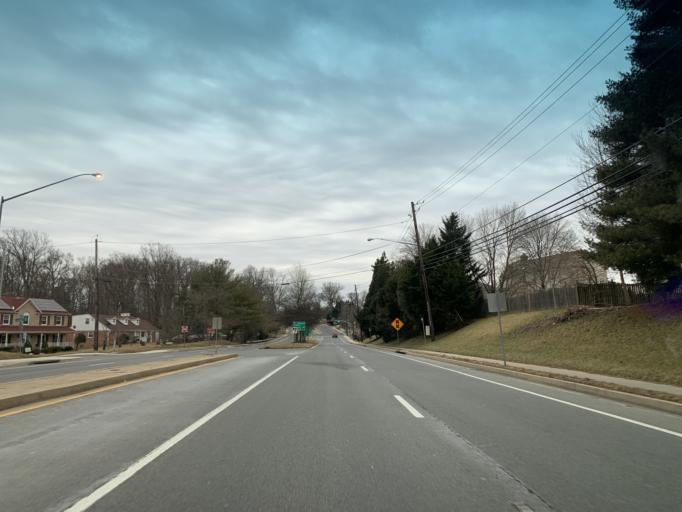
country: US
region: Maryland
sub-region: Montgomery County
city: Layhill
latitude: 39.0976
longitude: -77.0435
